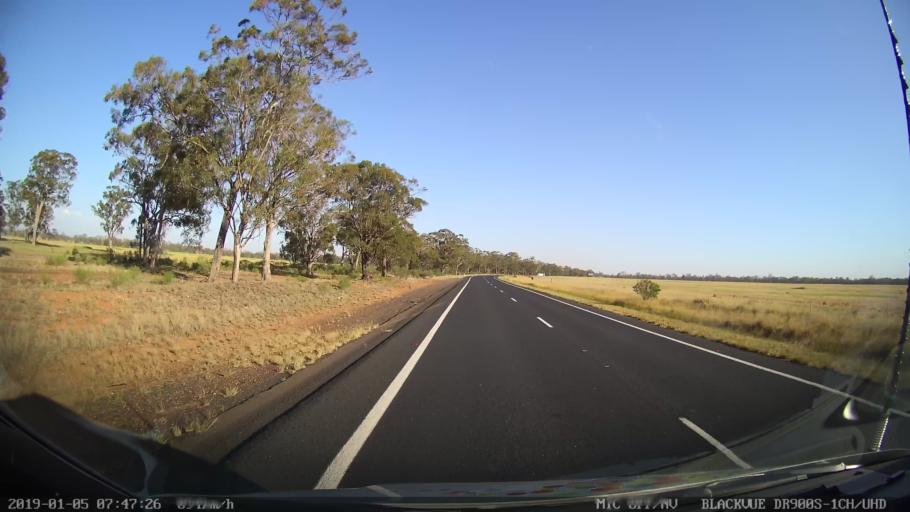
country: AU
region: New South Wales
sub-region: Gilgandra
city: Gilgandra
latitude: -31.8306
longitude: 148.6390
